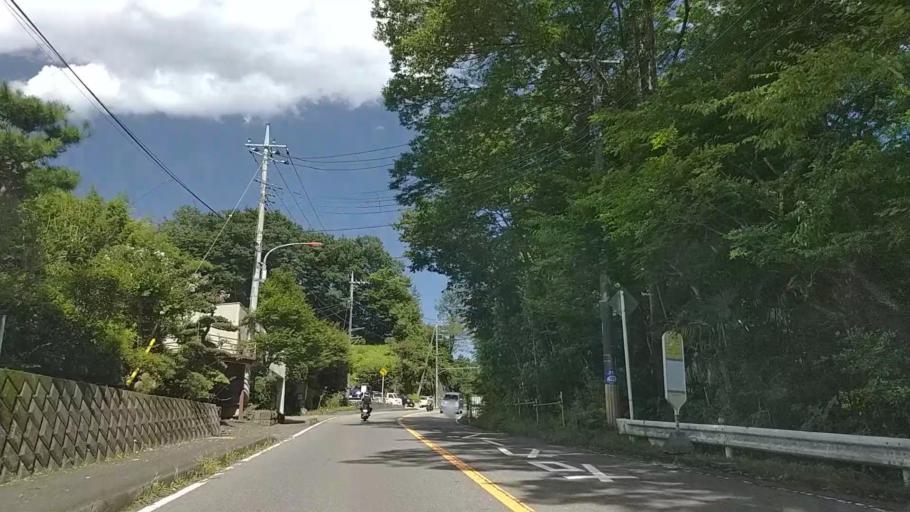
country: JP
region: Tokyo
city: Hachioji
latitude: 35.5674
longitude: 139.2738
